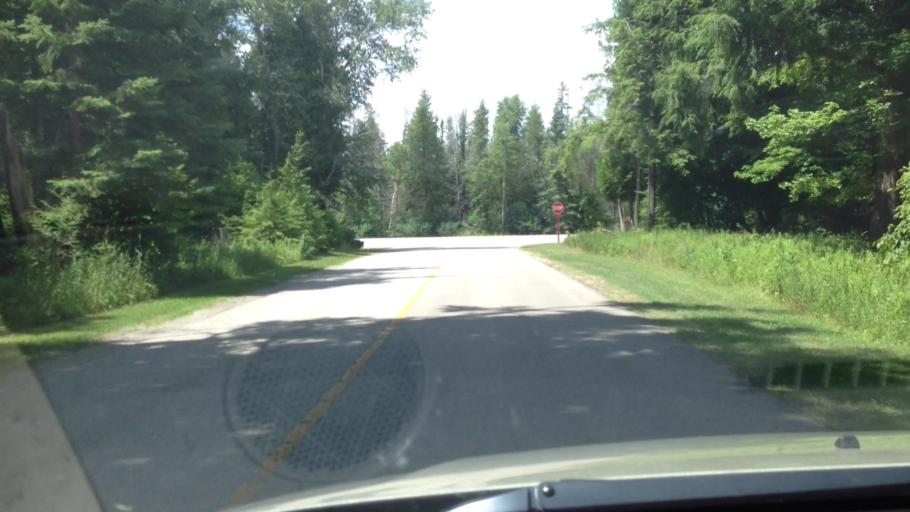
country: US
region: Michigan
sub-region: Menominee County
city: Menominee
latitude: 45.3951
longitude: -87.3664
